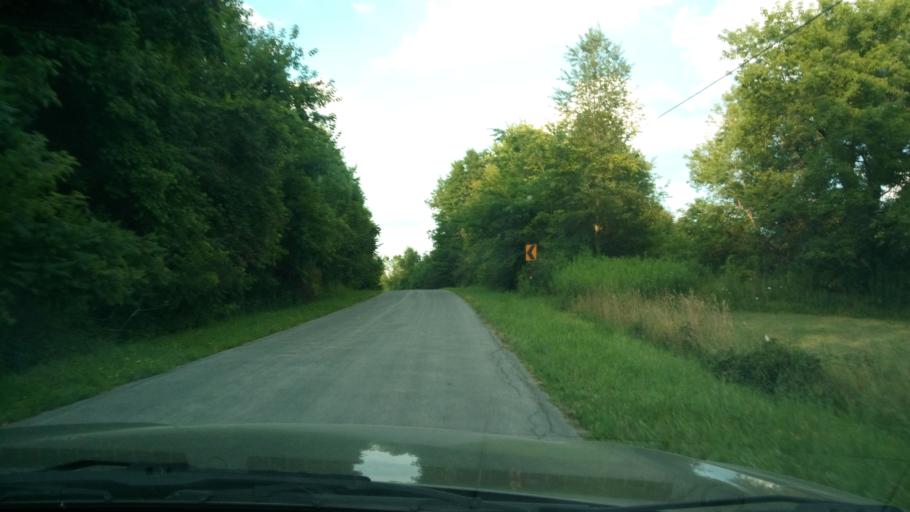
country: US
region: New York
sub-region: Wayne County
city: Clyde
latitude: 43.0805
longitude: -76.9229
